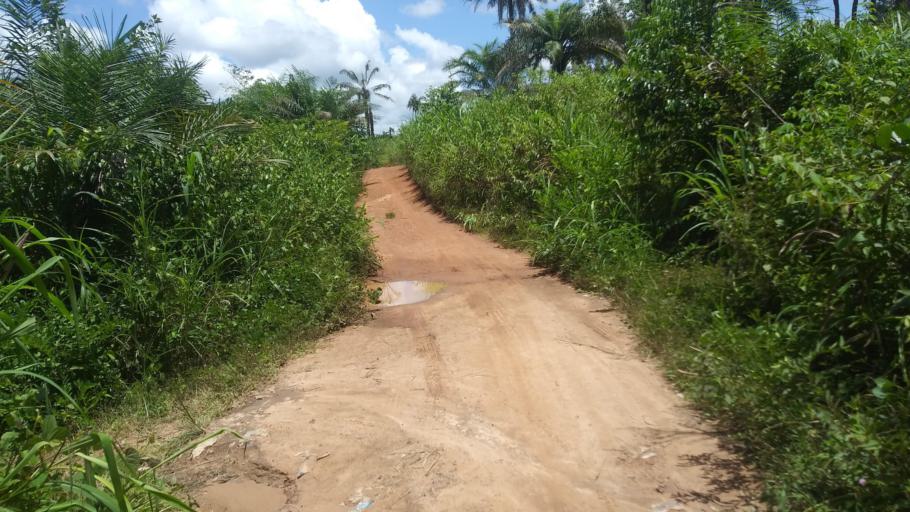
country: SL
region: Northern Province
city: Makeni
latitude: 8.8820
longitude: -12.0184
